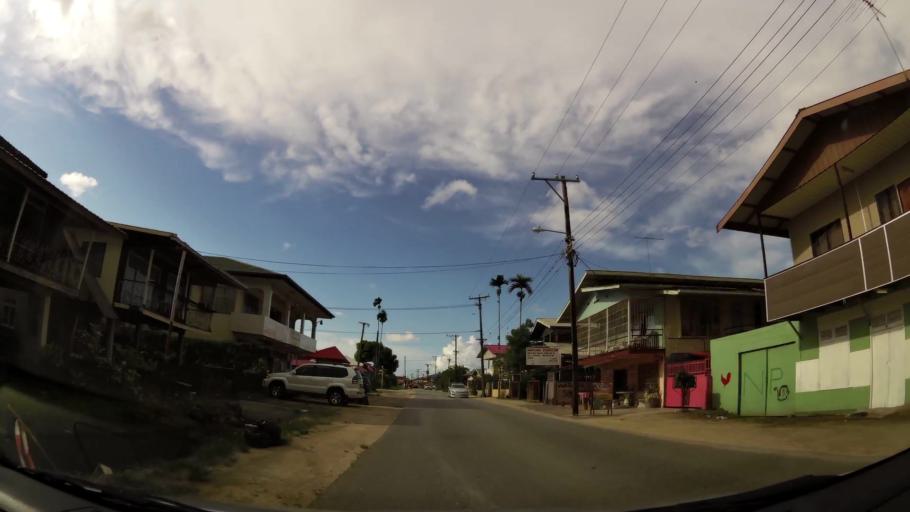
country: SR
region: Paramaribo
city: Paramaribo
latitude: 5.8408
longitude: -55.1819
